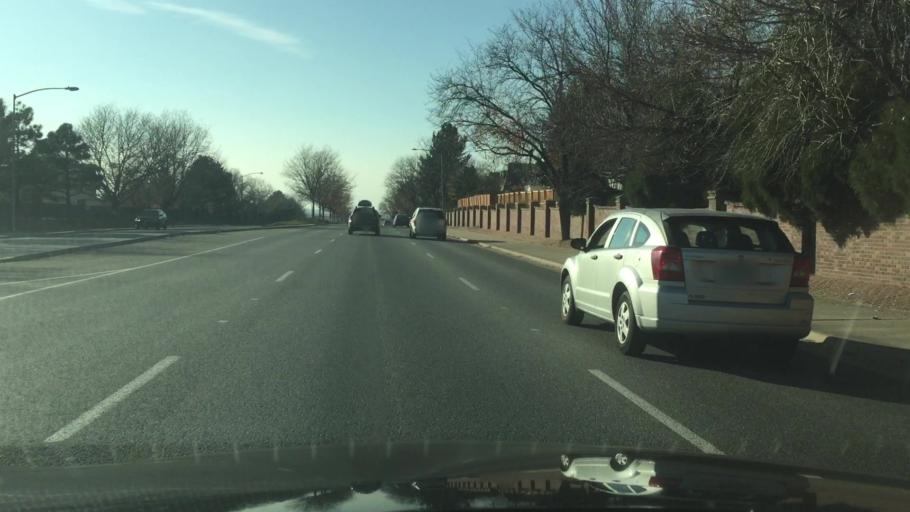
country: US
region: Colorado
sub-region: Arapahoe County
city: Dove Valley
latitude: 39.6532
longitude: -104.8241
